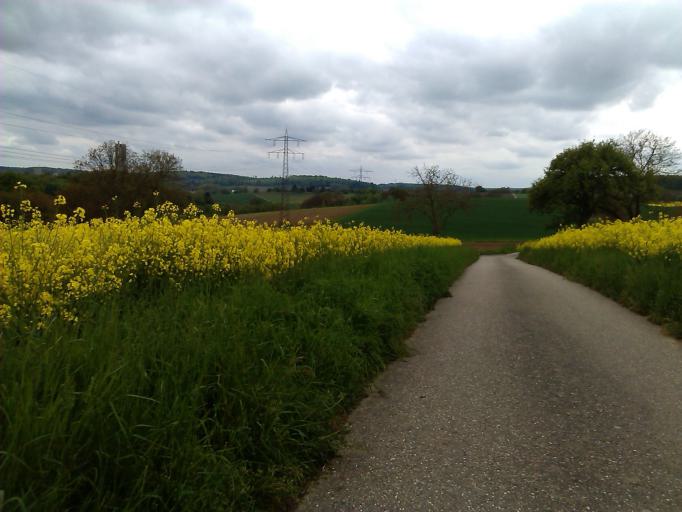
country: DE
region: Baden-Wuerttemberg
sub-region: Karlsruhe Region
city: Woessingen
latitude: 49.0241
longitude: 8.6307
